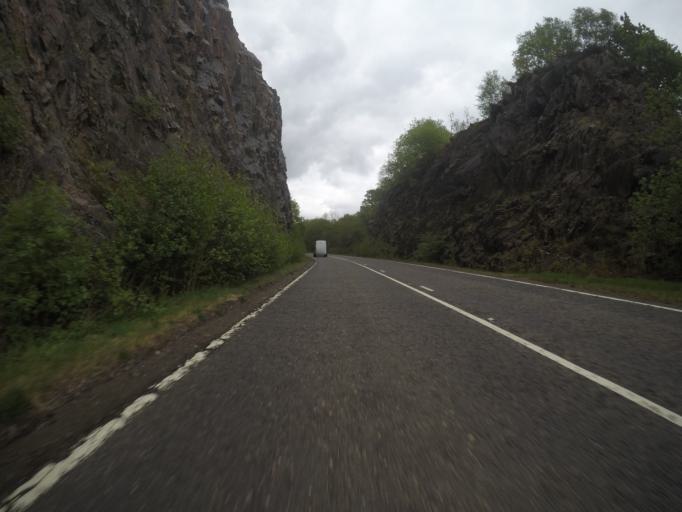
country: GB
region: Scotland
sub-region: Highland
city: Fort William
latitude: 57.2589
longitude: -5.4902
